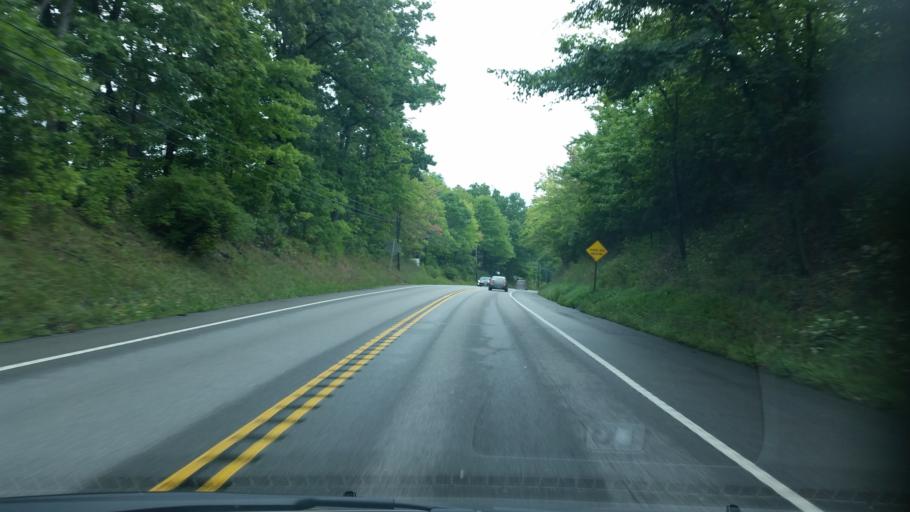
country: US
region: Pennsylvania
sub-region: Clearfield County
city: Shiloh
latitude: 40.9564
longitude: -78.2956
